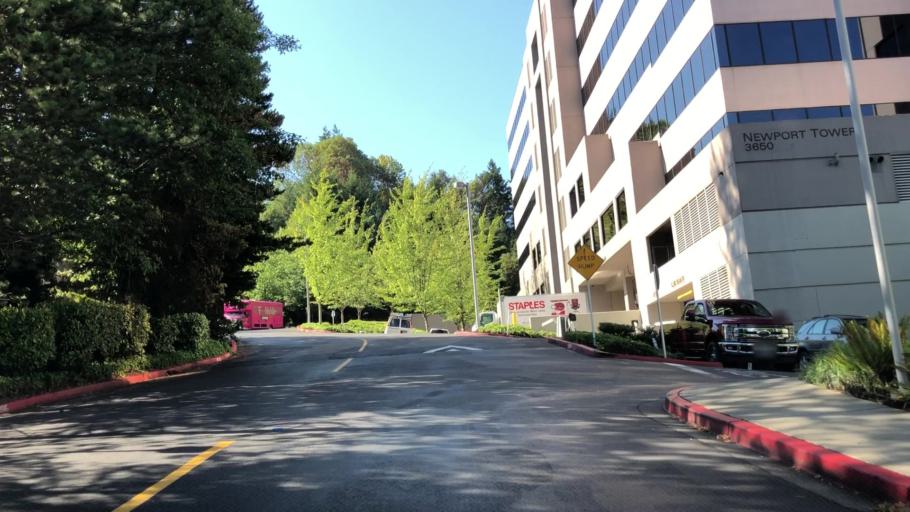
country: US
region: Washington
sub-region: King County
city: Newport
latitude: 47.5786
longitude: -122.1645
